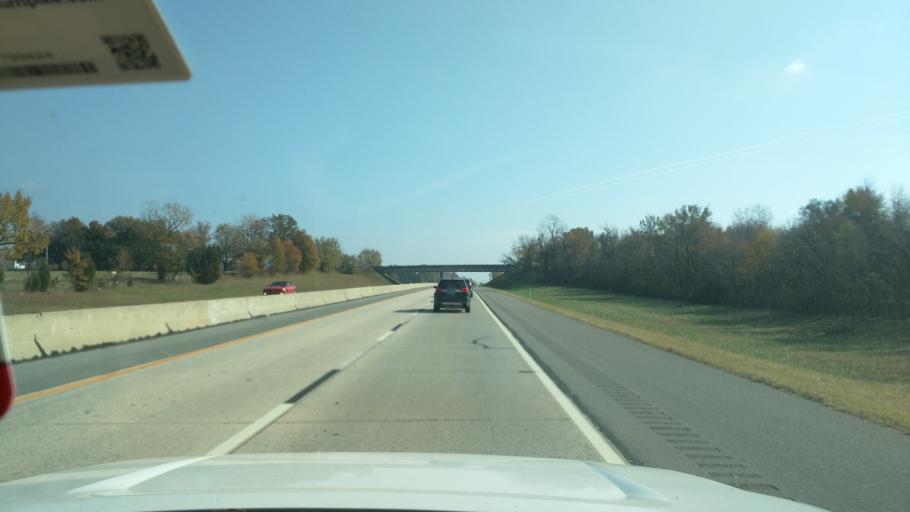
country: US
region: Oklahoma
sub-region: Muskogee County
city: Muskogee
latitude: 35.8288
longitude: -95.3508
